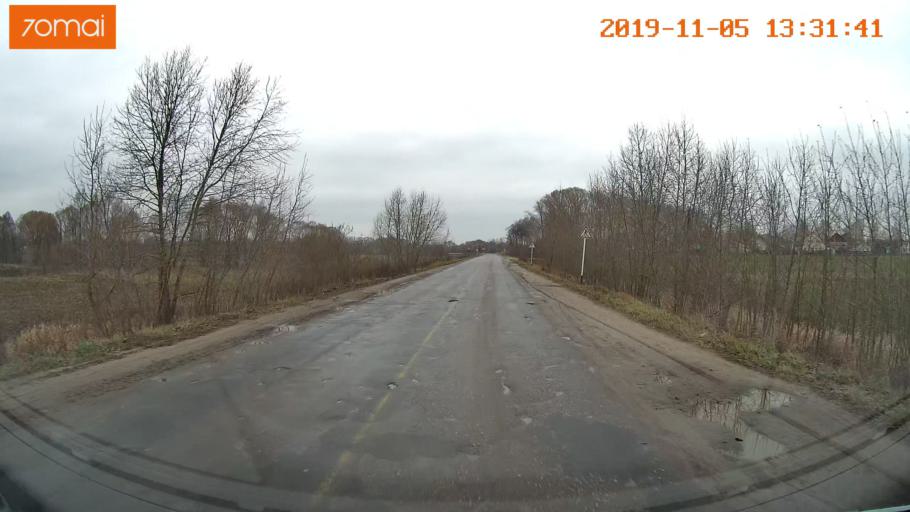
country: RU
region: Ivanovo
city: Shuya
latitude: 56.8781
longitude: 41.3940
